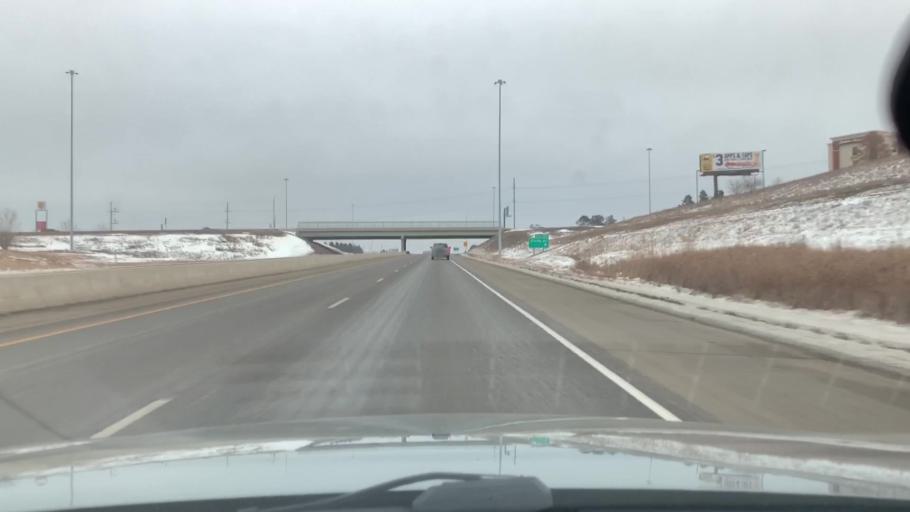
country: US
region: North Dakota
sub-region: Burleigh County
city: Bismarck
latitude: 46.8264
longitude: -100.8189
